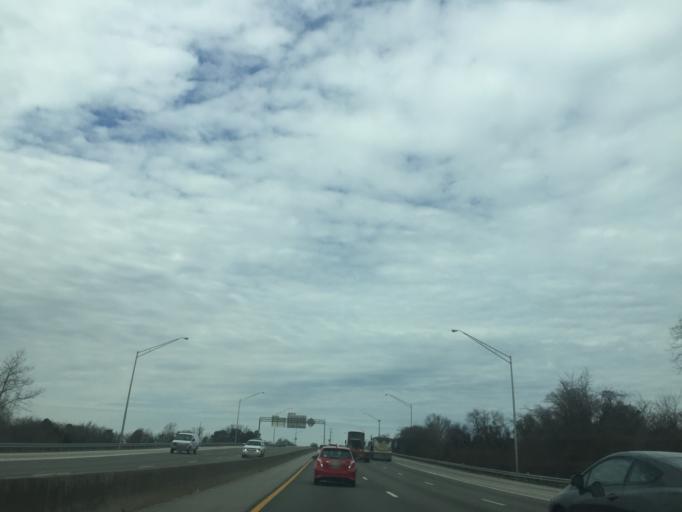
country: US
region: Virginia
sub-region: City of Hampton
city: East Hampton
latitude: 37.0253
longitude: -76.3308
